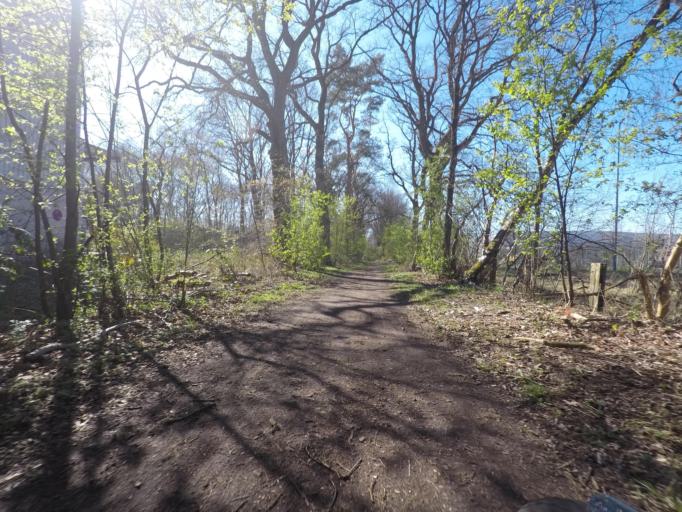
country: DE
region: Hamburg
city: Langenhorn
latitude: 53.6597
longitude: 9.9784
